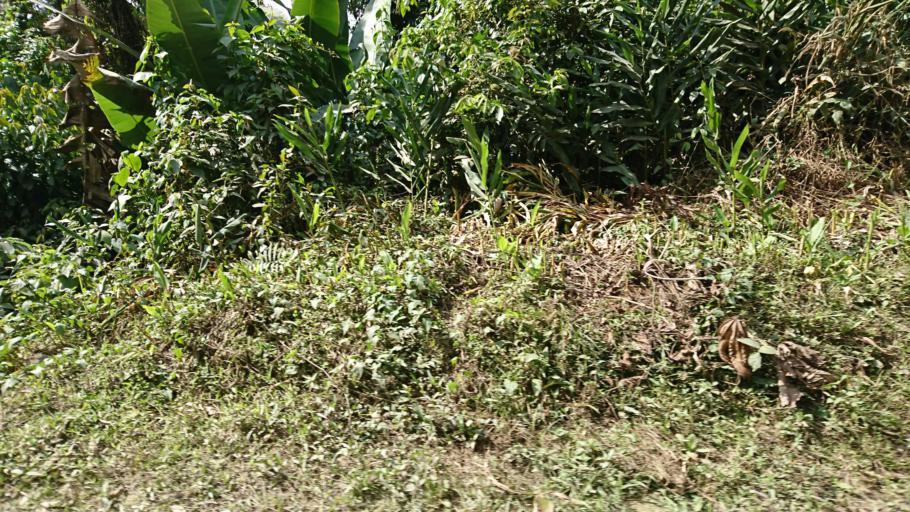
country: BO
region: La Paz
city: Coroico
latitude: -16.1210
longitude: -67.7650
